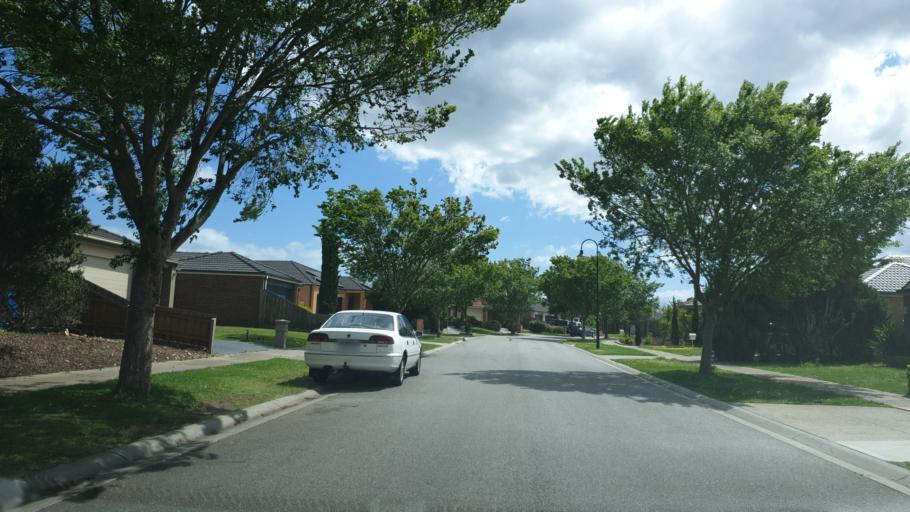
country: AU
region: Victoria
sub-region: Casey
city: Cranbourne
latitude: -38.0942
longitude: 145.2867
